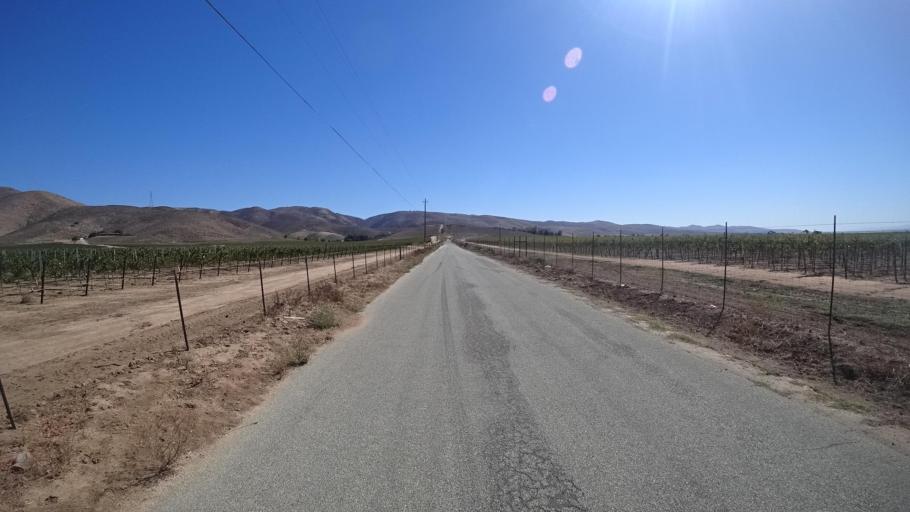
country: US
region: California
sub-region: Monterey County
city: Soledad
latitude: 36.4455
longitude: -121.3088
